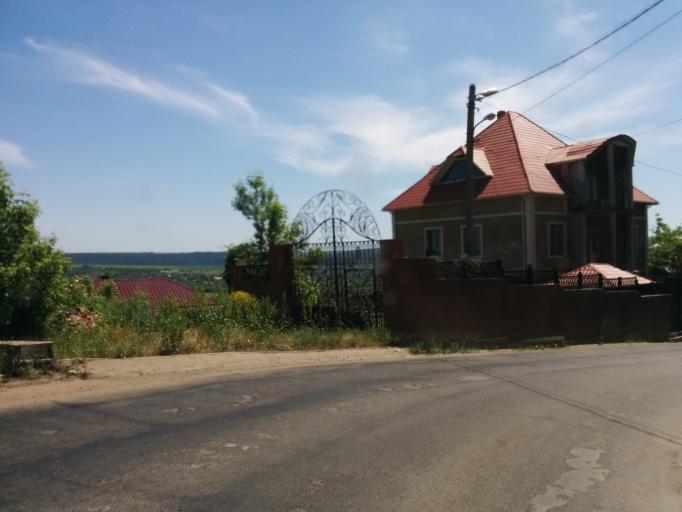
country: MD
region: Raionul Soroca
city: Soroca
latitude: 48.1608
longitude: 28.2955
